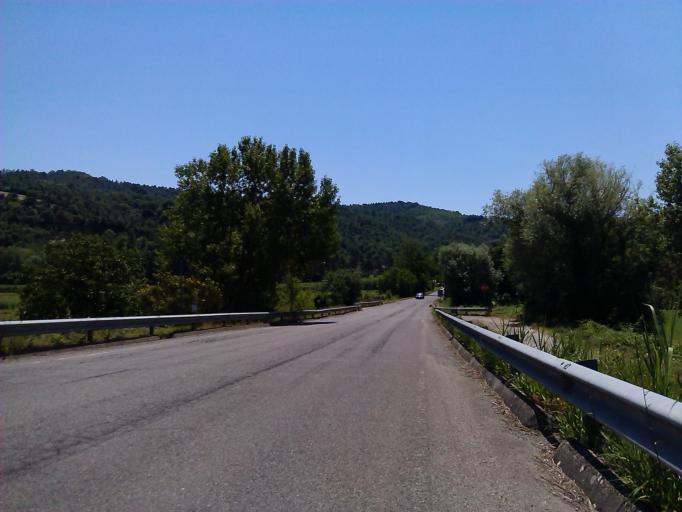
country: IT
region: Umbria
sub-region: Provincia di Terni
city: Fabro Scalo
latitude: 42.8677
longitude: 12.0472
